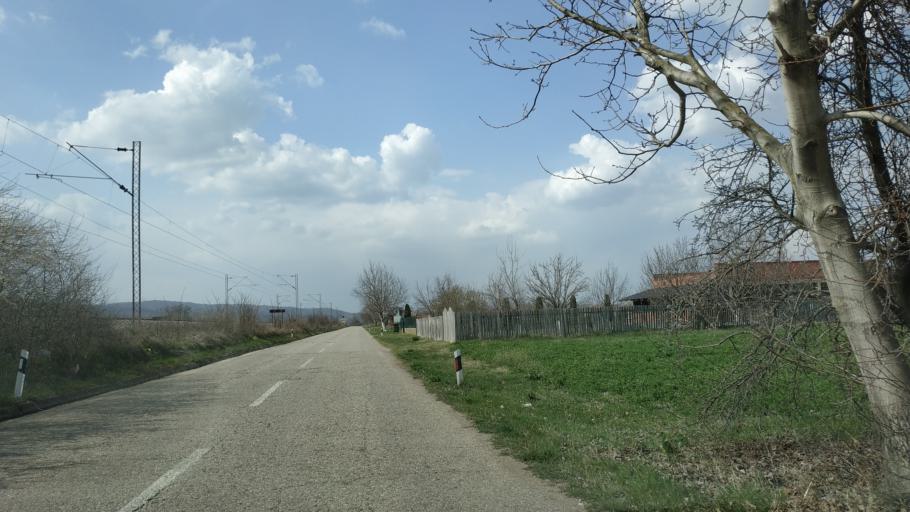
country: RS
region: Central Serbia
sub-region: Nisavski Okrug
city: Razanj
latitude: 43.5697
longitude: 21.5878
